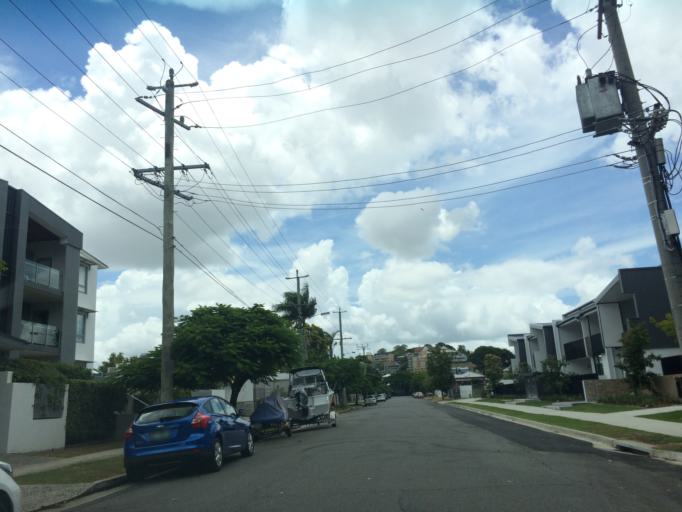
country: AU
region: Queensland
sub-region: Brisbane
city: Ascot
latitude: -27.4451
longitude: 153.0577
